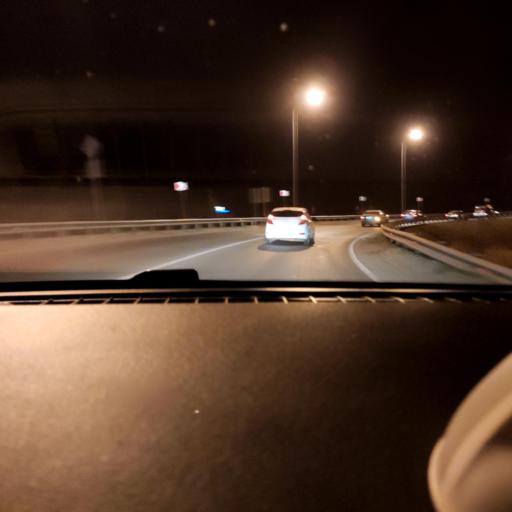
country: RU
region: Samara
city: Petra-Dubrava
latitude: 53.3222
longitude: 50.2956
